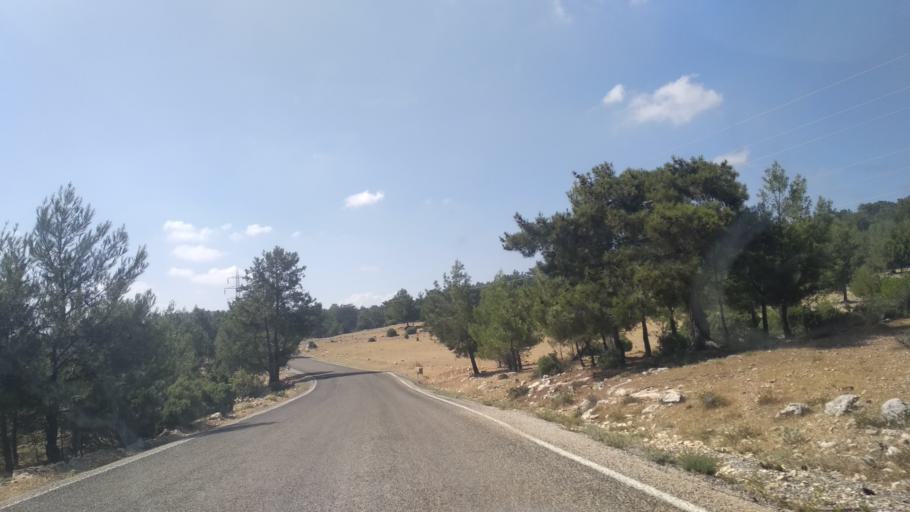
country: TR
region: Mersin
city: Gulnar
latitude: 36.3001
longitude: 33.4629
